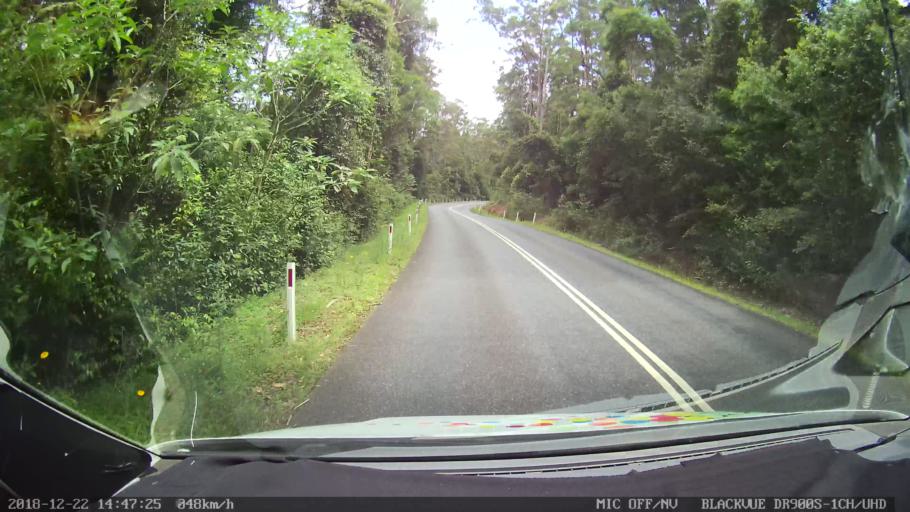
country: AU
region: New South Wales
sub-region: Bellingen
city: Dorrigo
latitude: -30.1757
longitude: 152.5564
